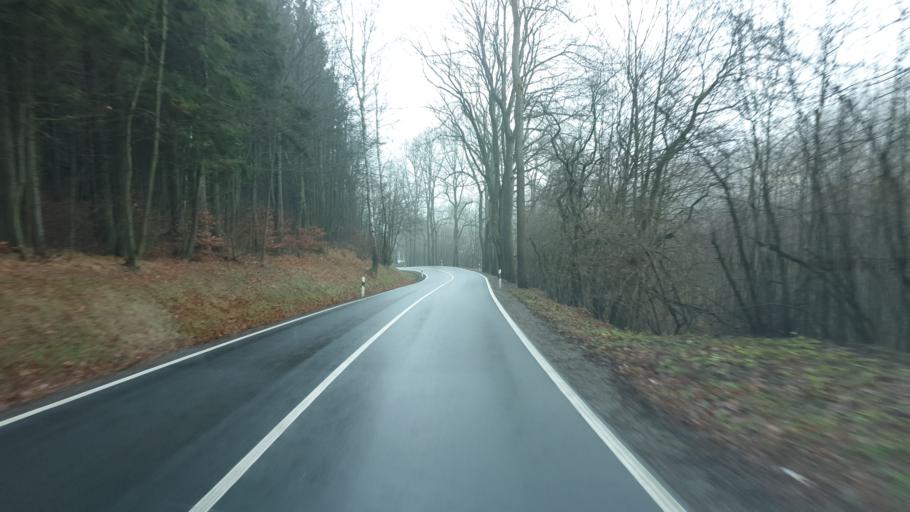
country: DE
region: Saxony
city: Neuhausen
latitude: 50.6837
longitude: 13.4603
